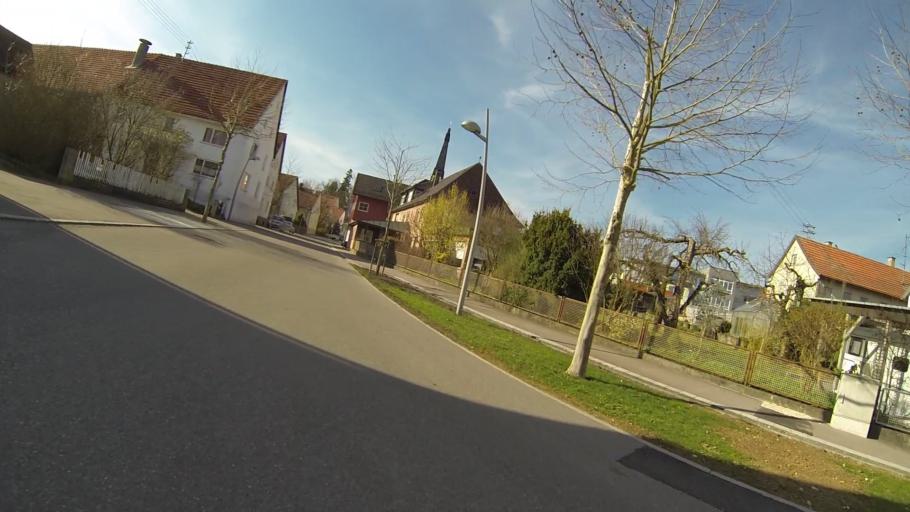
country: DE
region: Baden-Wuerttemberg
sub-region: Regierungsbezirk Stuttgart
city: Niederstotzingen
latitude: 48.5400
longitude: 10.2329
